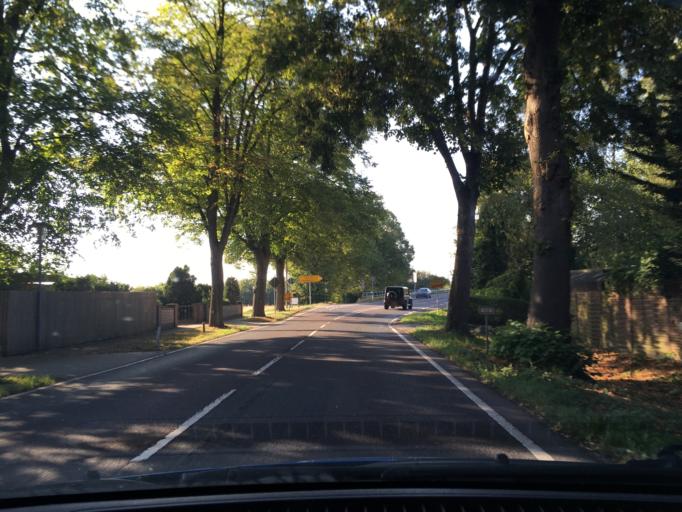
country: DE
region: Lower Saxony
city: Burgdorf
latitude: 52.4691
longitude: 9.9705
